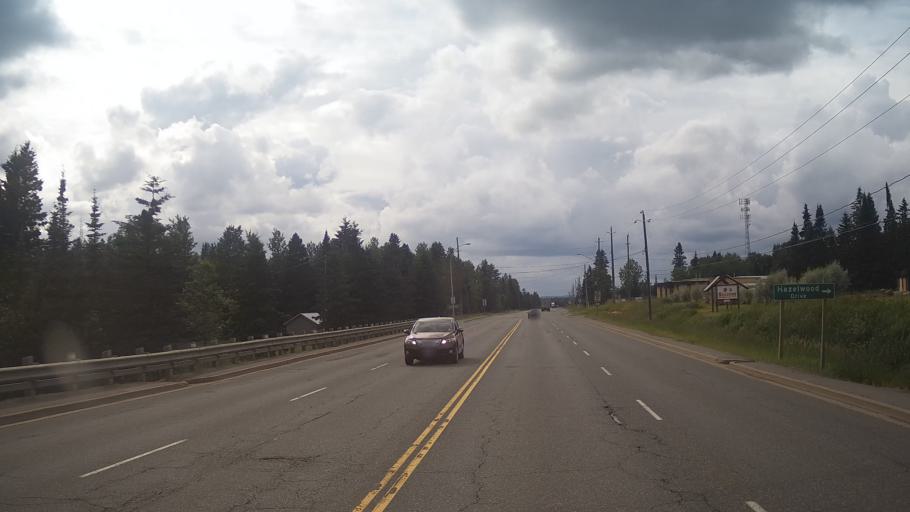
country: CA
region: Ontario
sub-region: Thunder Bay District
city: Thunder Bay
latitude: 48.4624
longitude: -89.2778
